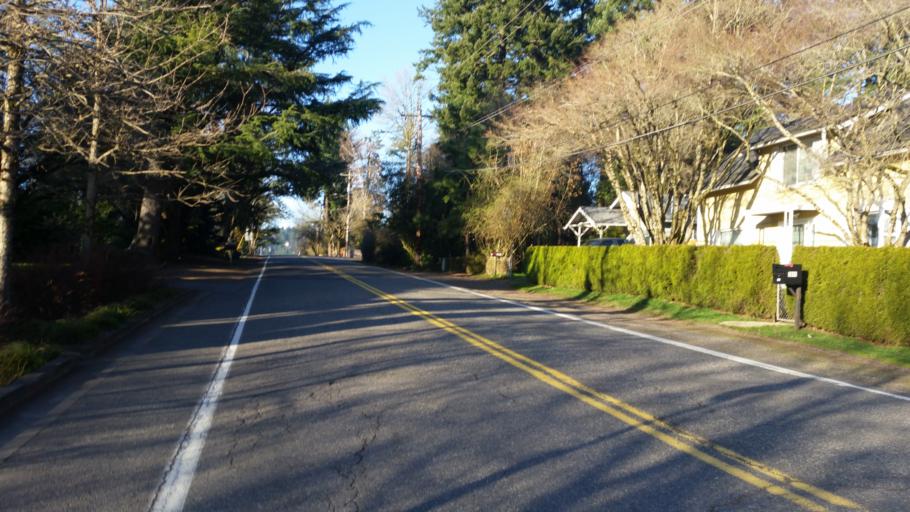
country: US
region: Oregon
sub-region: Washington County
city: Raleigh Hills
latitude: 45.4813
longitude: -122.7232
